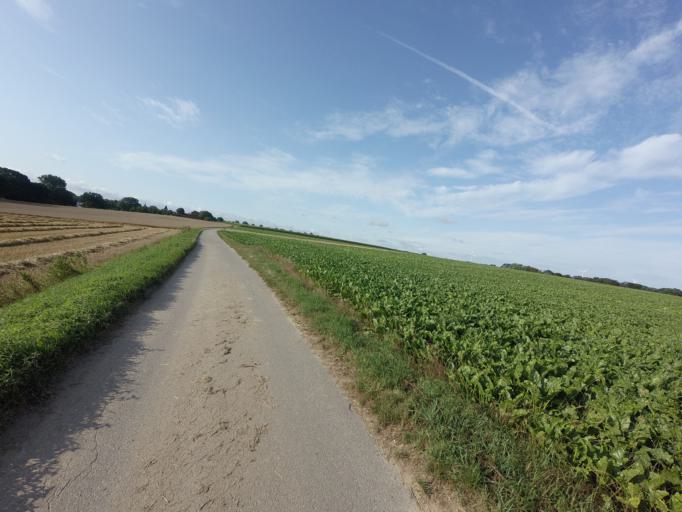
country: DE
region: North Rhine-Westphalia
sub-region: Regierungsbezirk Koln
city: Alsdorf
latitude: 50.8492
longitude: 6.1714
